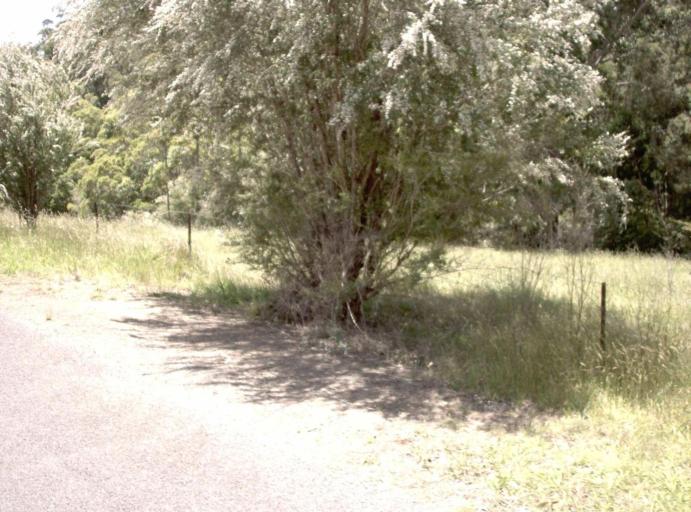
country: AU
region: New South Wales
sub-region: Bombala
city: Bombala
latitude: -37.5220
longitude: 148.9327
